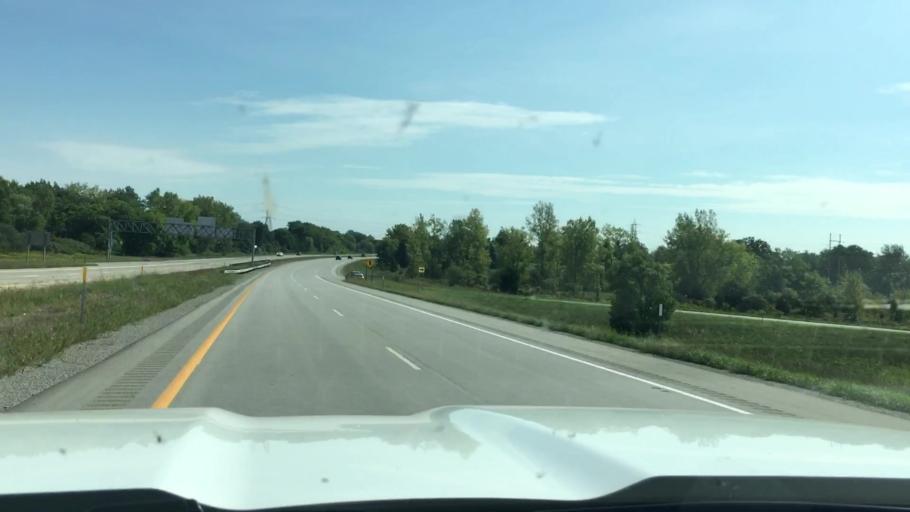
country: US
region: Michigan
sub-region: Bay County
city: Bay City
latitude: 43.5961
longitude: -83.9458
